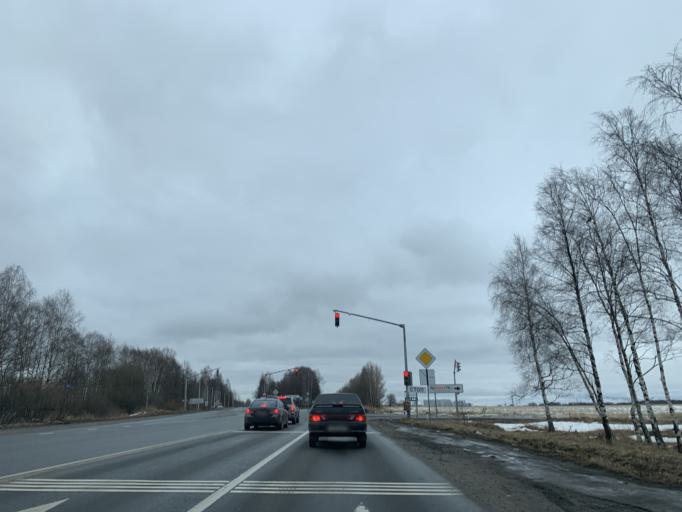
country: RU
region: Jaroslavl
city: Yaroslavl
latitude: 57.7305
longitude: 39.7400
